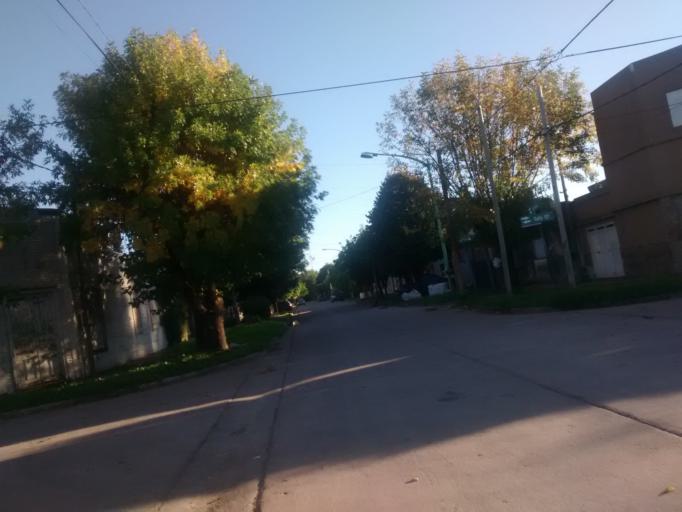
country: AR
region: Buenos Aires
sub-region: Partido de La Plata
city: La Plata
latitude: -34.8965
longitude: -57.9323
